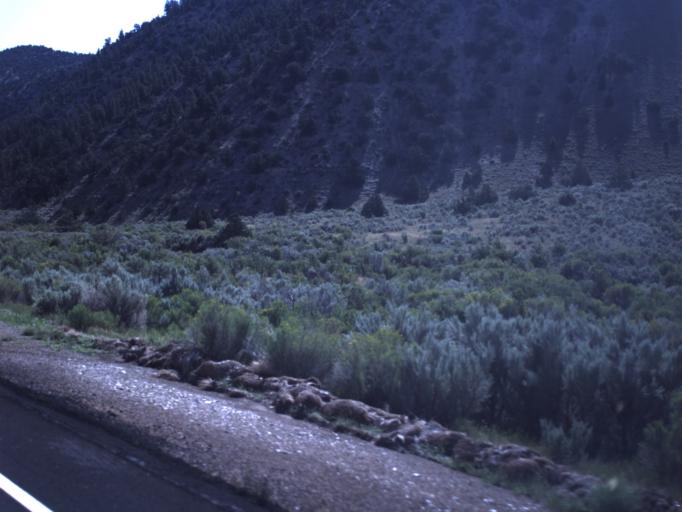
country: US
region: Utah
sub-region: Duchesne County
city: Duchesne
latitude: 40.0033
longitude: -110.5785
